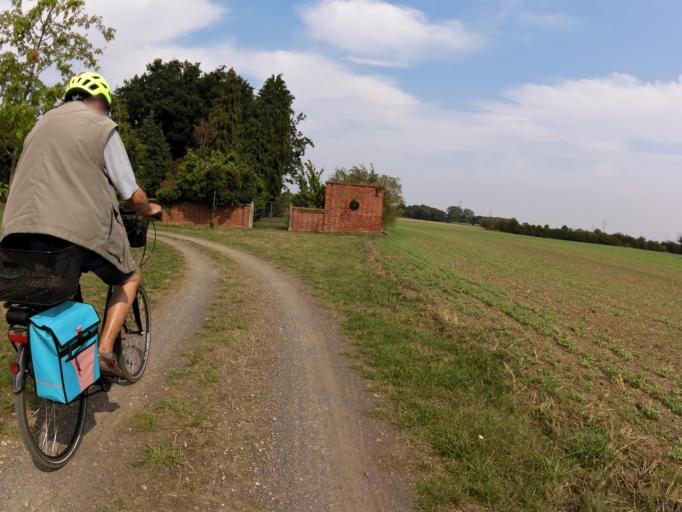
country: DE
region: Lower Saxony
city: Stolzenau
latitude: 52.5284
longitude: 9.0776
